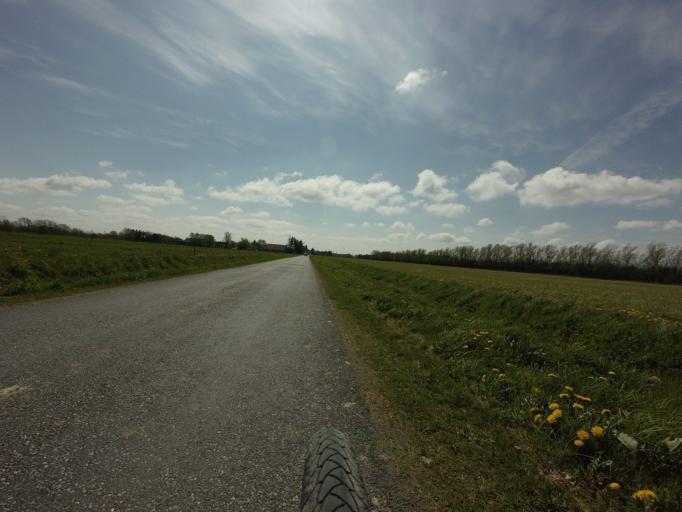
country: DK
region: North Denmark
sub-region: Jammerbugt Kommune
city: Brovst
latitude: 57.1521
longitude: 9.5538
